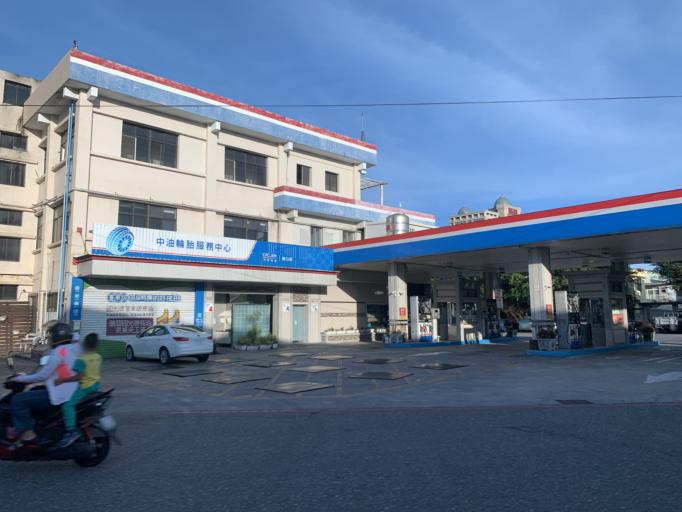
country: TW
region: Taiwan
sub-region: Hualien
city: Hualian
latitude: 23.9977
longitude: 121.6311
